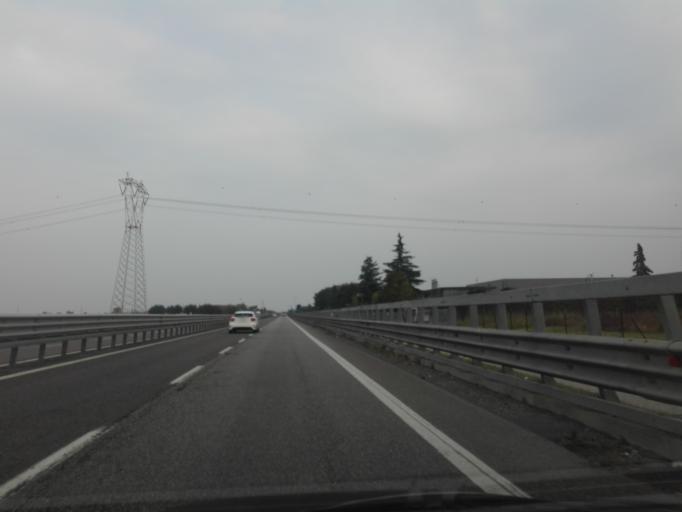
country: IT
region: Veneto
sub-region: Provincia di Verona
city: Vallese
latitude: 45.3412
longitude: 11.0693
